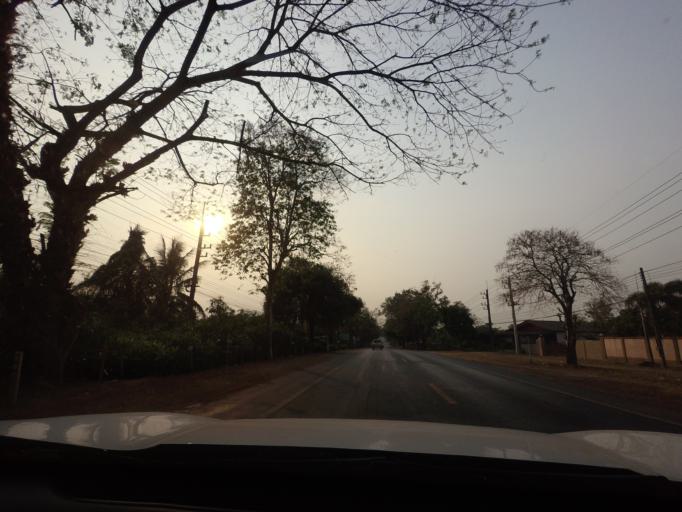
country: TH
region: Nakhon Nayok
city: Pak Phli
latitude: 14.1494
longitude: 101.3324
